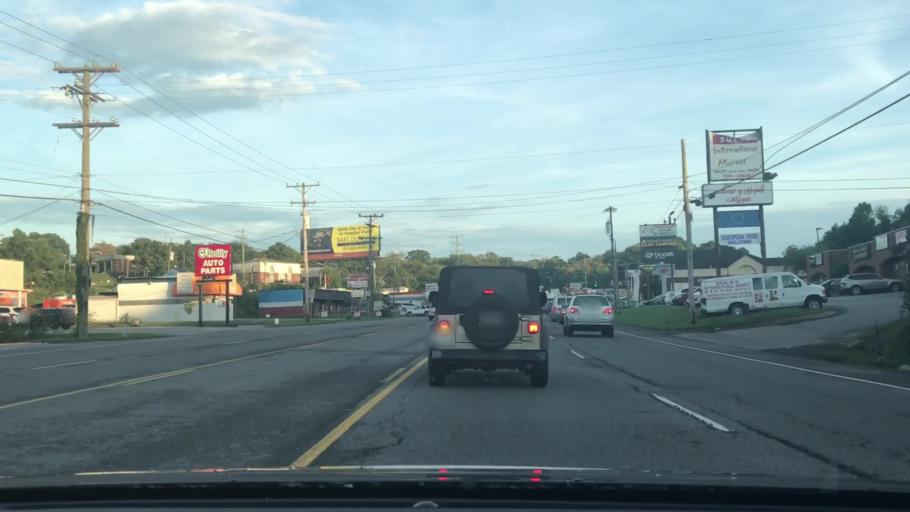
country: US
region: Tennessee
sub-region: Davidson County
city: Oak Hill
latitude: 36.0693
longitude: -86.7205
